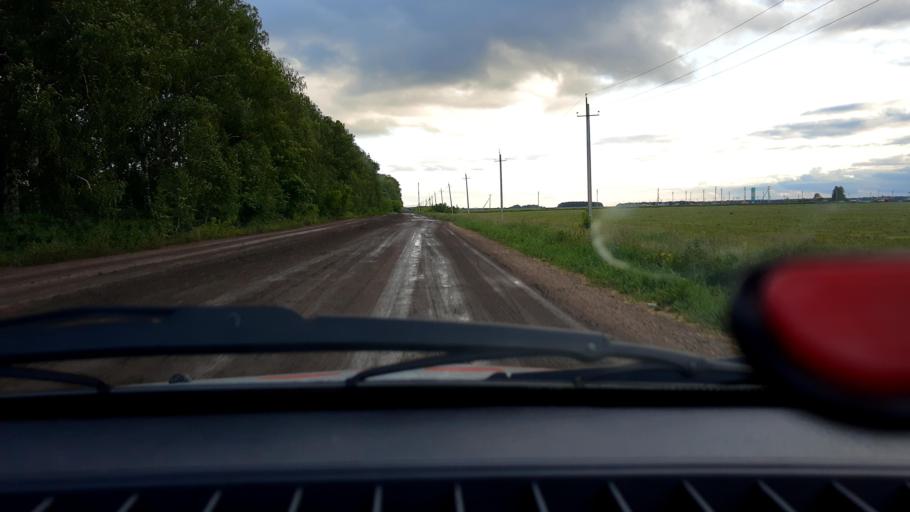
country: RU
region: Bashkortostan
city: Tolbazy
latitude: 54.1923
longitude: 55.8805
